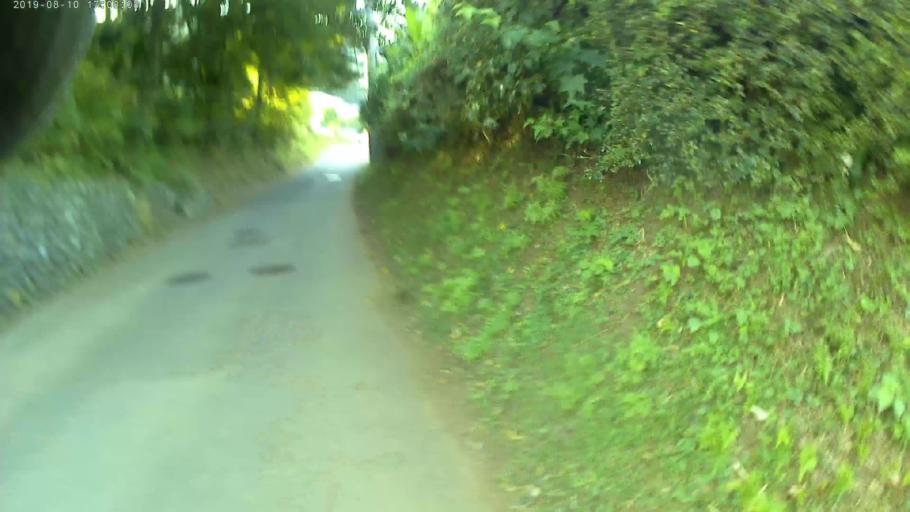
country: JP
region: Yamanashi
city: Uenohara
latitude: 35.6231
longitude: 139.1691
